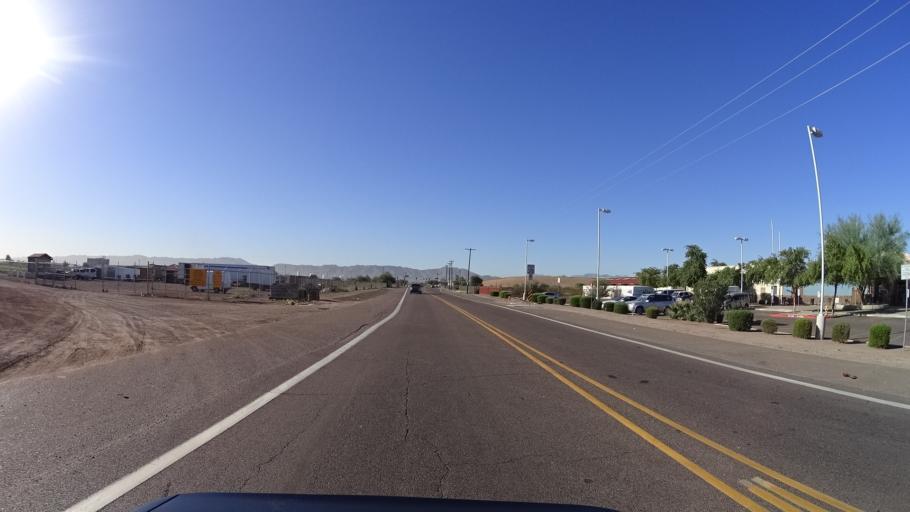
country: US
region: Arizona
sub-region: Maricopa County
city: Phoenix
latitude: 33.4250
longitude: -112.1171
